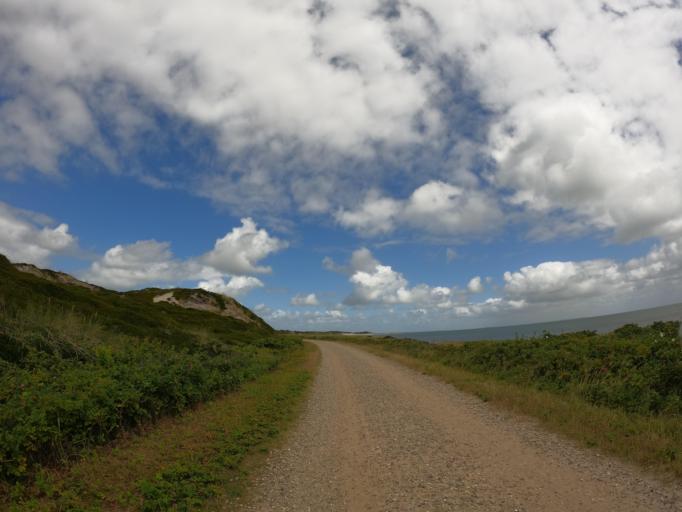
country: DE
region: Schleswig-Holstein
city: Tinnum
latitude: 54.7932
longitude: 8.2936
